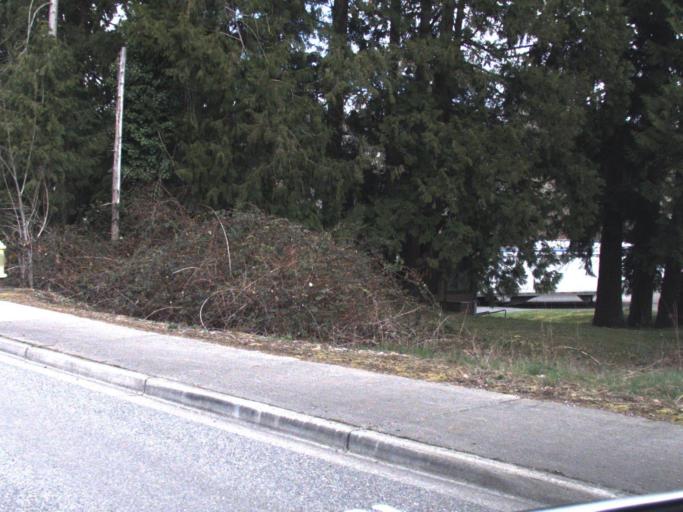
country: US
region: Washington
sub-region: Pierce County
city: Edgewood
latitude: 47.2578
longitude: -122.2949
